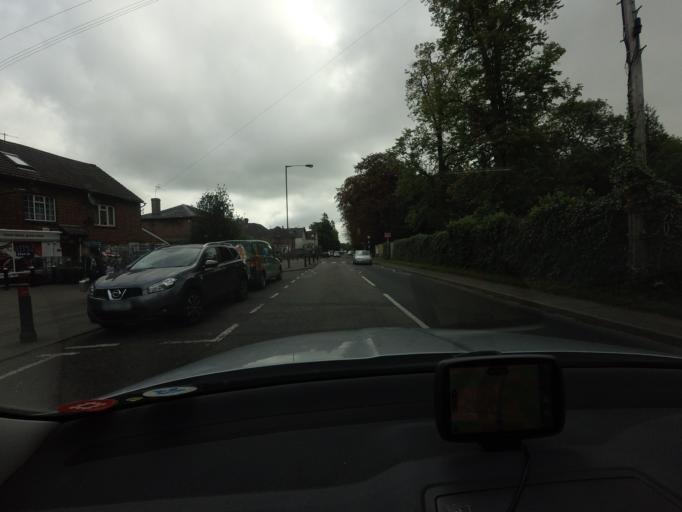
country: GB
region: England
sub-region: Kent
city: Tonbridge
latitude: 51.2168
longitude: 0.2399
